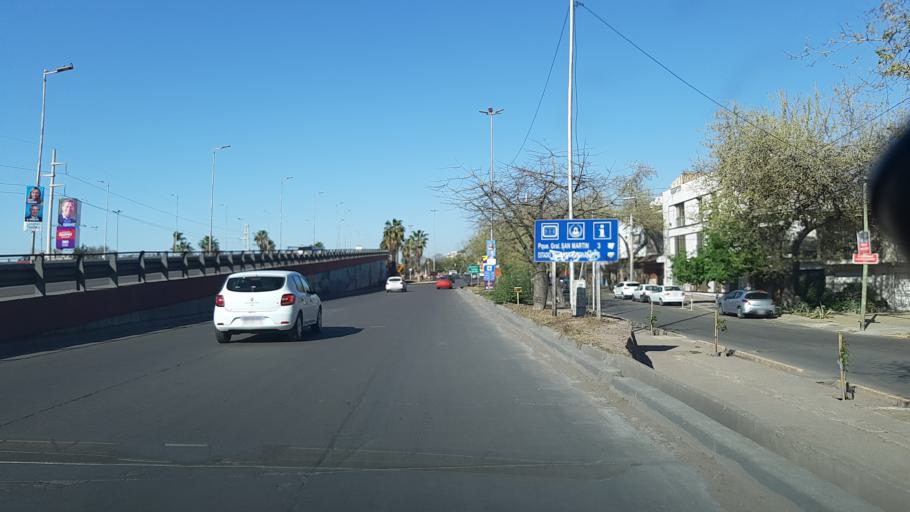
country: AR
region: Mendoza
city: Mendoza
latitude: -32.8942
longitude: -68.8321
